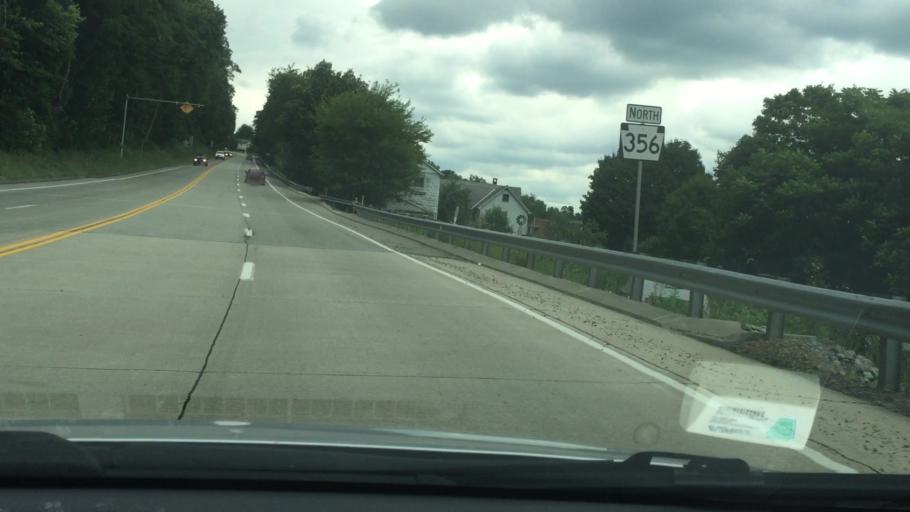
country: US
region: Pennsylvania
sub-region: Armstrong County
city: Freeport
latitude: 40.6767
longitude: -79.6923
